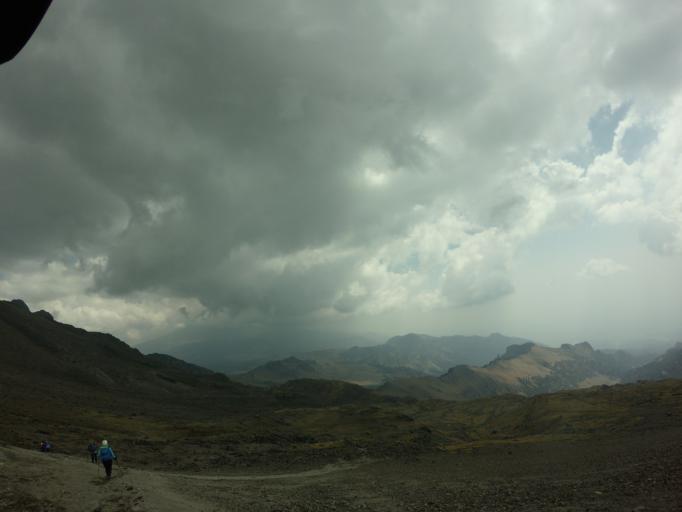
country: MX
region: Mexico
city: Amecameca de Juarez
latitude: 19.1595
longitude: -98.6451
